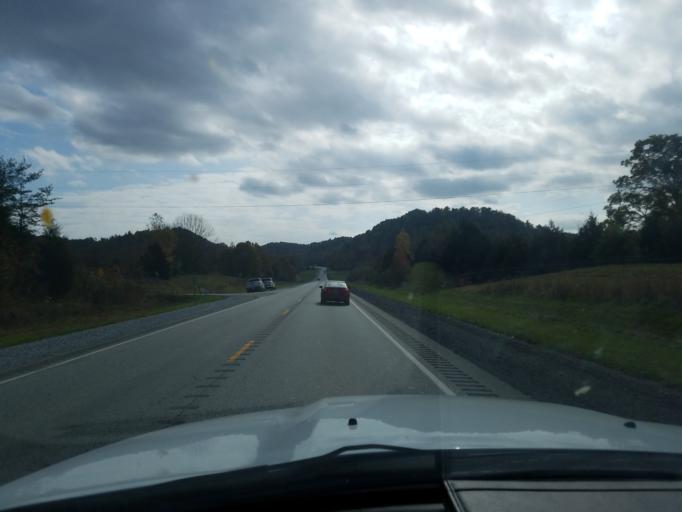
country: US
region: Kentucky
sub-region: Marion County
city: Lebanon
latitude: 37.4610
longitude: -85.2971
